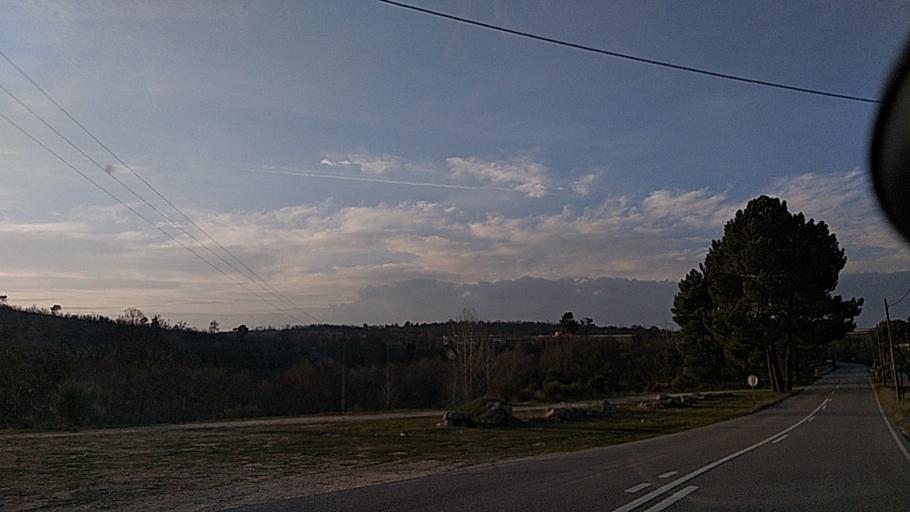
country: PT
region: Guarda
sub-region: Pinhel
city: Pinhel
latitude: 40.6005
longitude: -7.0317
